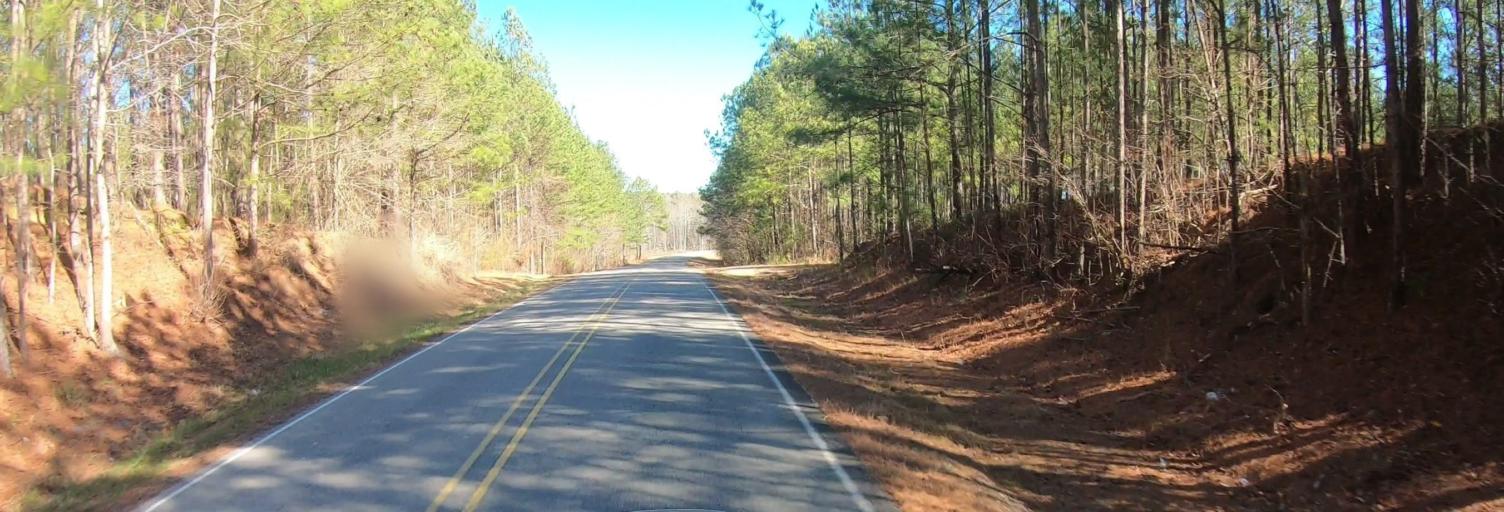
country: US
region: Alabama
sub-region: Clay County
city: Ashland
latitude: 33.3708
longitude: -85.8914
